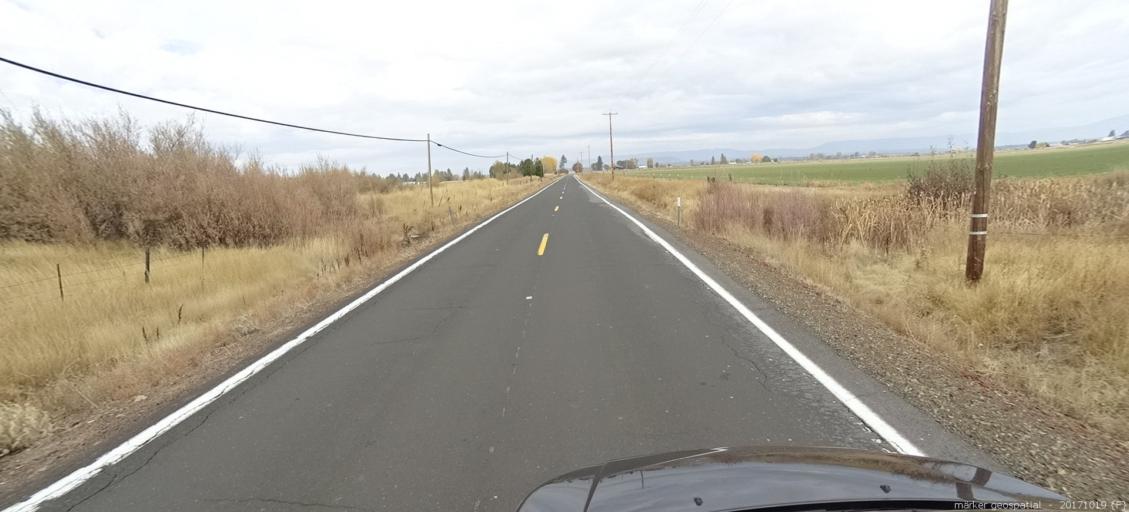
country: US
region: California
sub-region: Shasta County
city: Burney
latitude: 41.0698
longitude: -121.5092
